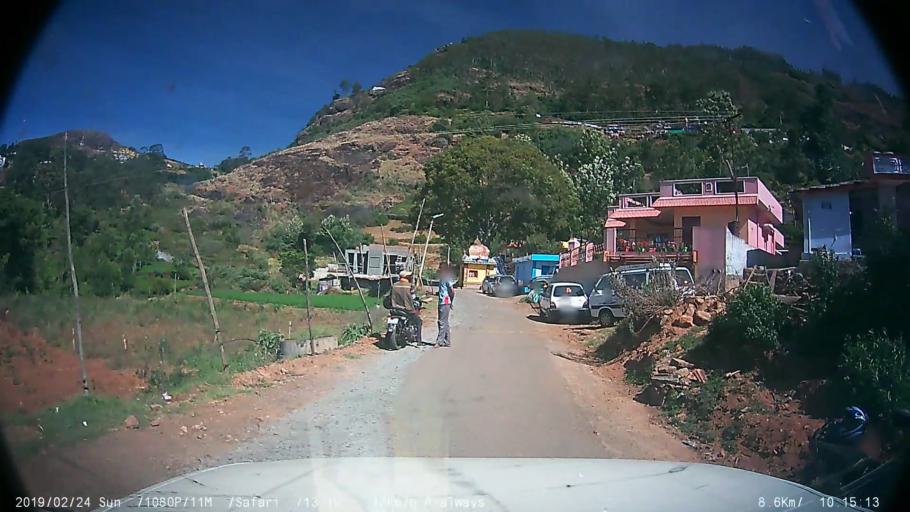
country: IN
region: Tamil Nadu
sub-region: Nilgiri
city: Aravankadu
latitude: 11.3853
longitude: 76.7247
